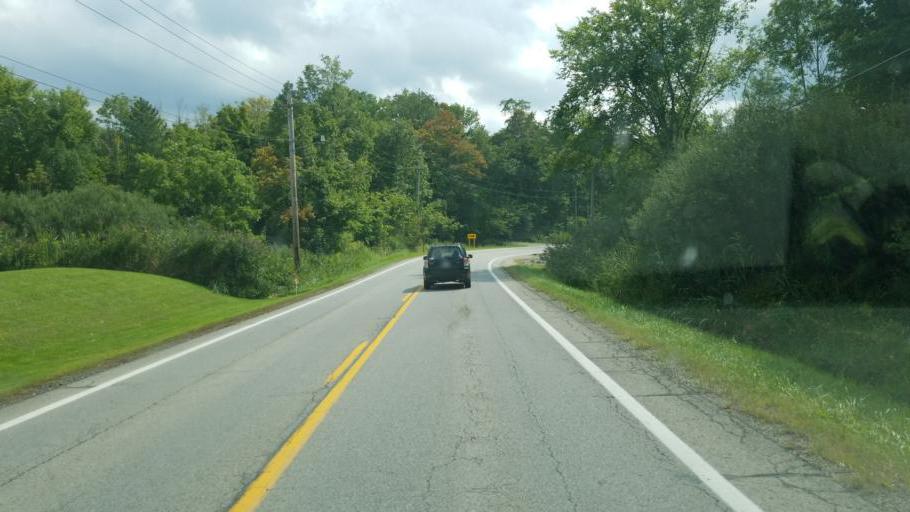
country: US
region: Ohio
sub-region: Geauga County
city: Burton
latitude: 41.4639
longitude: -81.1937
